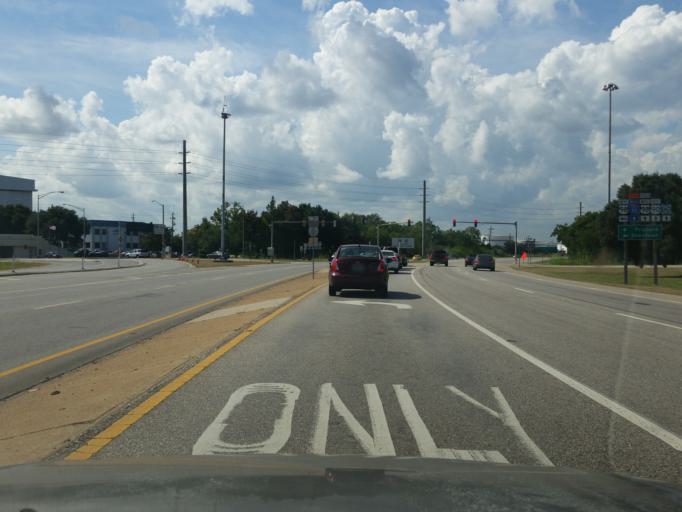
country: US
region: Alabama
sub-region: Mobile County
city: Mobile
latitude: 30.6926
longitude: -88.0290
